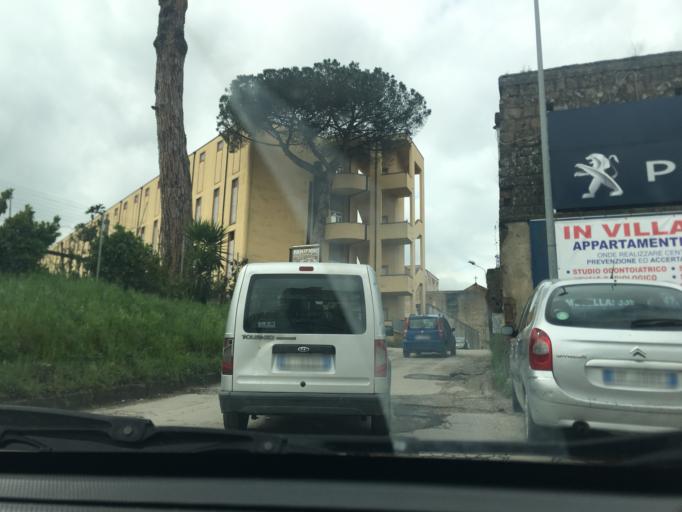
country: IT
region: Campania
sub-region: Provincia di Napoli
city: Mugnano di Napoli
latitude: 40.8950
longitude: 14.2010
